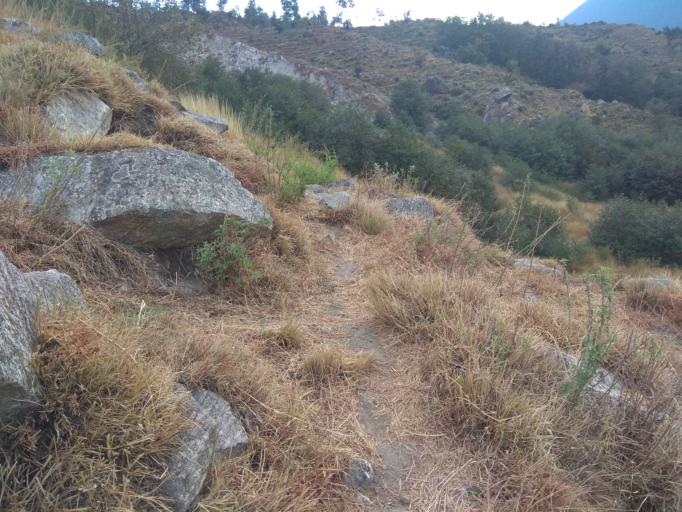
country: NP
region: Far Western
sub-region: Seti Zone
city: Achham
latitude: 29.2325
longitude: 81.6430
